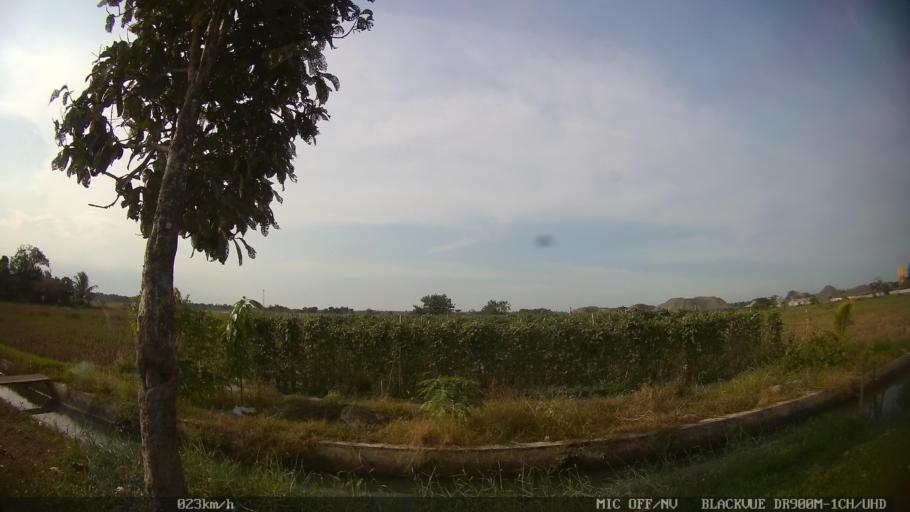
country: ID
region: North Sumatra
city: Binjai
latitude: 3.6212
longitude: 98.5304
